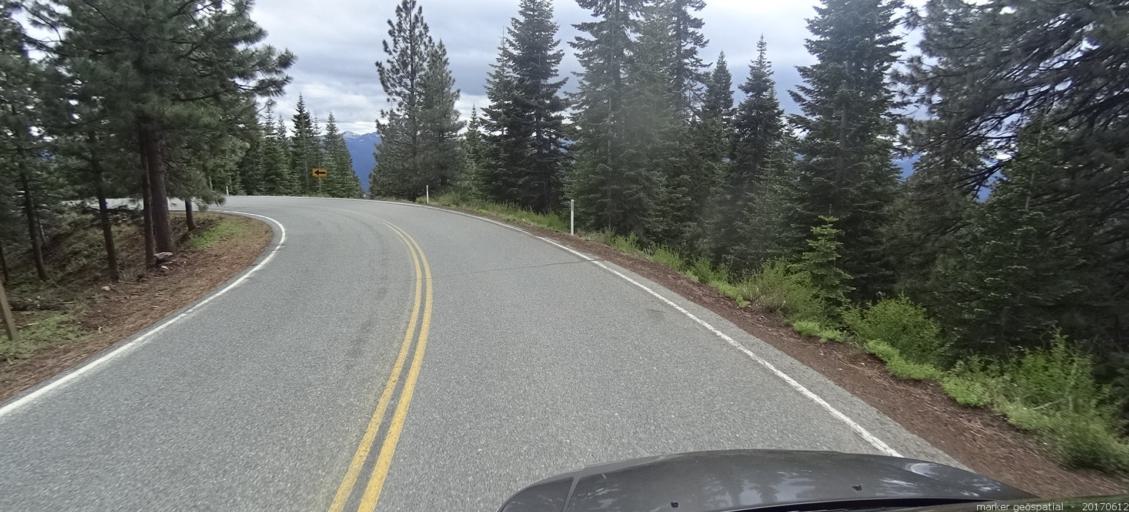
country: US
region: California
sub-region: Siskiyou County
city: Mount Shasta
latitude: 41.3393
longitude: -122.2596
